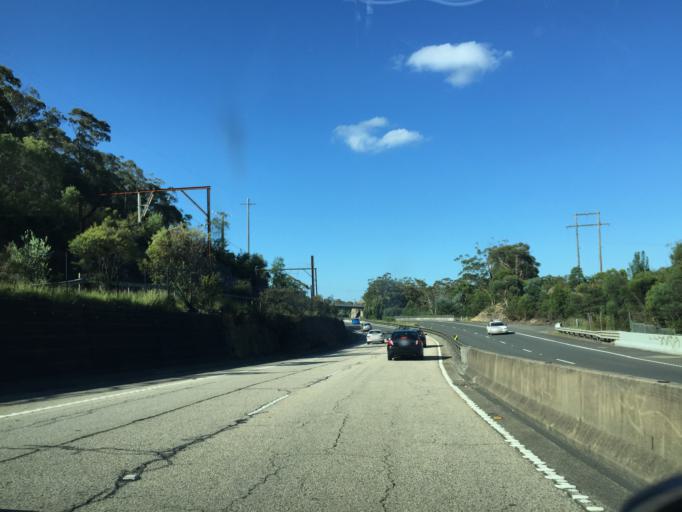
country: AU
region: New South Wales
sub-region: Blue Mountains Municipality
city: Hazelbrook
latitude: -33.7199
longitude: 150.4948
